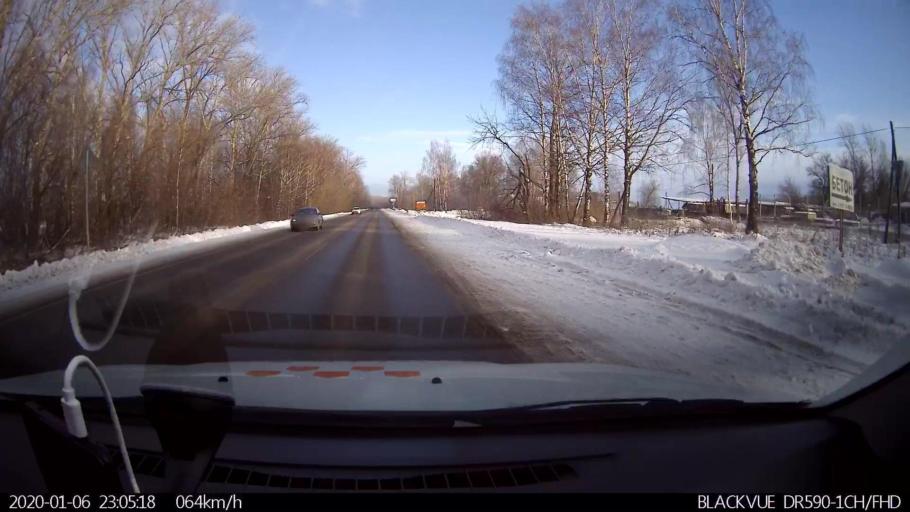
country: RU
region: Nizjnij Novgorod
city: Bogorodsk
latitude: 56.1205
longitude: 43.5537
